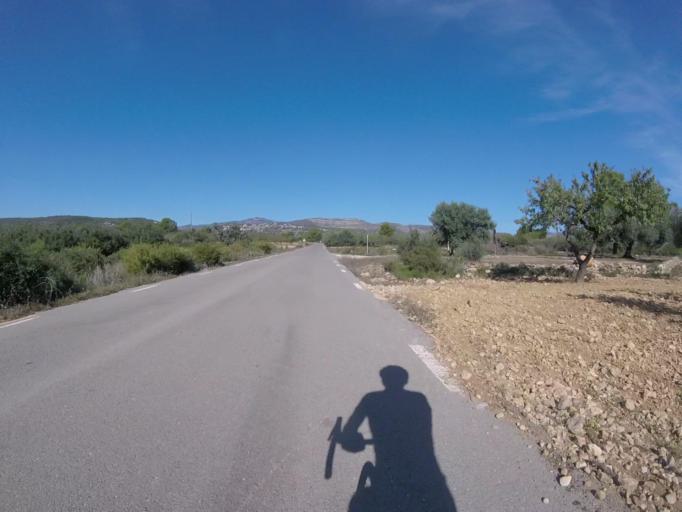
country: ES
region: Valencia
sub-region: Provincia de Castello
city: Sarratella
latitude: 40.2703
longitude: 0.0598
